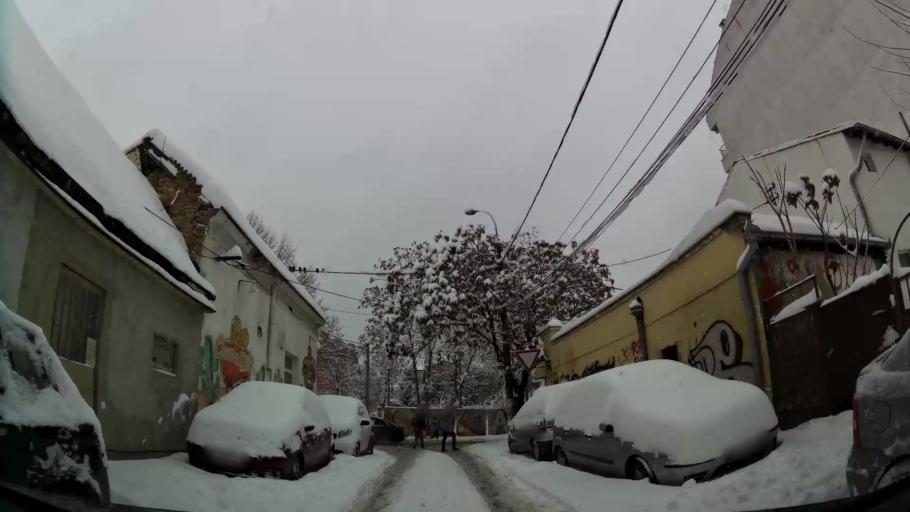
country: RS
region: Central Serbia
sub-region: Belgrade
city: Vracar
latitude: 44.7901
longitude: 20.4797
